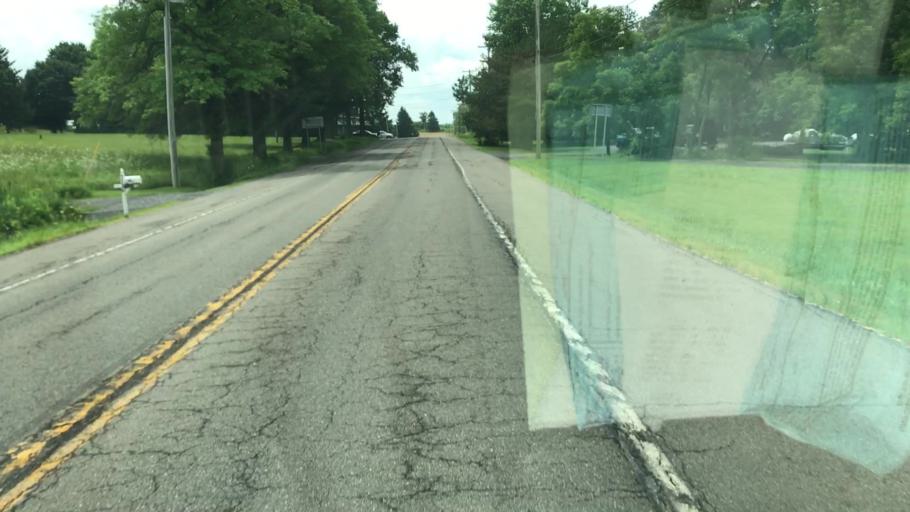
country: US
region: New York
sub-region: Onondaga County
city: Manlius
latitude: 42.8955
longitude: -76.0314
